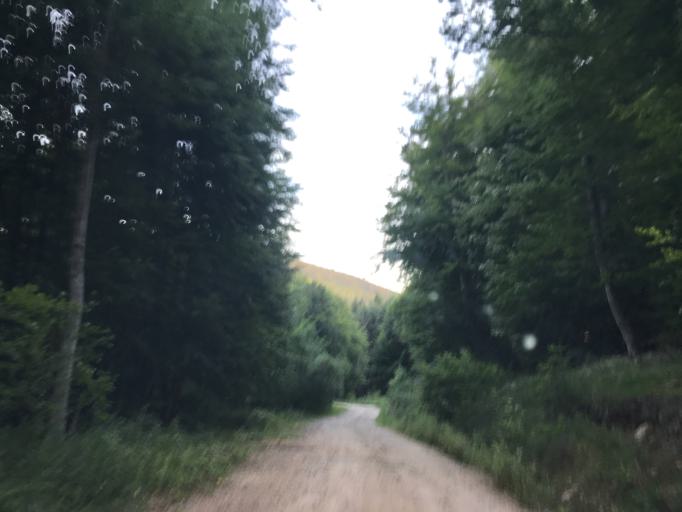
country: FR
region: Rhone-Alpes
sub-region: Departement de la Loire
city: Noiretable
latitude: 45.8032
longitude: 3.7050
